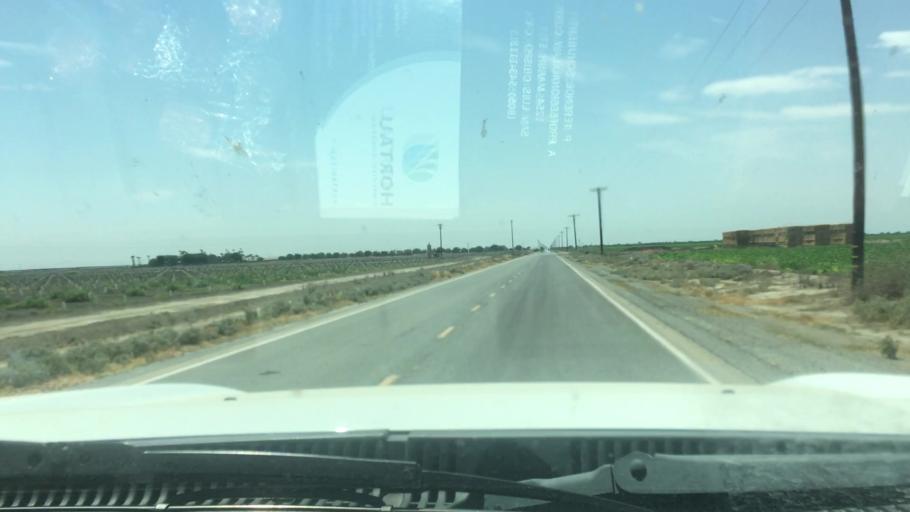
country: US
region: California
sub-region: Tulare County
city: Tipton
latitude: 36.0510
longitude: -119.4349
